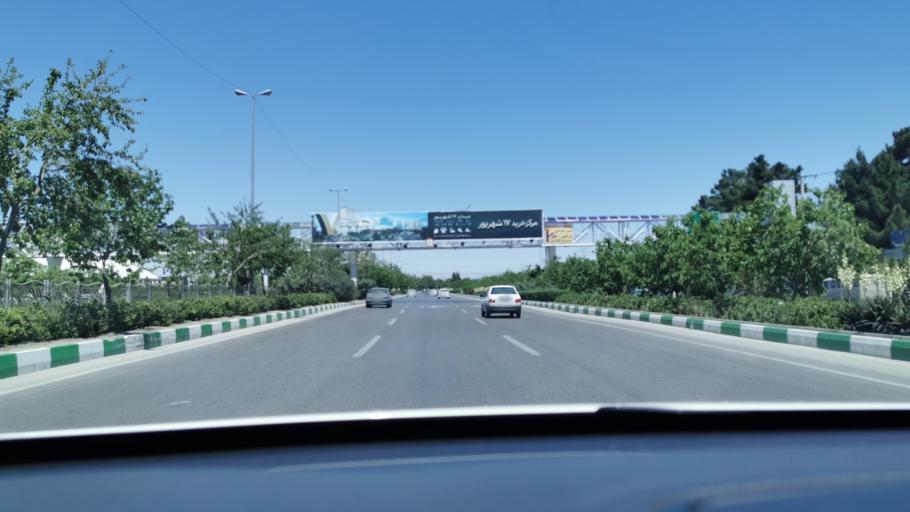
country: IR
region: Razavi Khorasan
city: Mashhad
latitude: 36.2553
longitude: 59.6193
